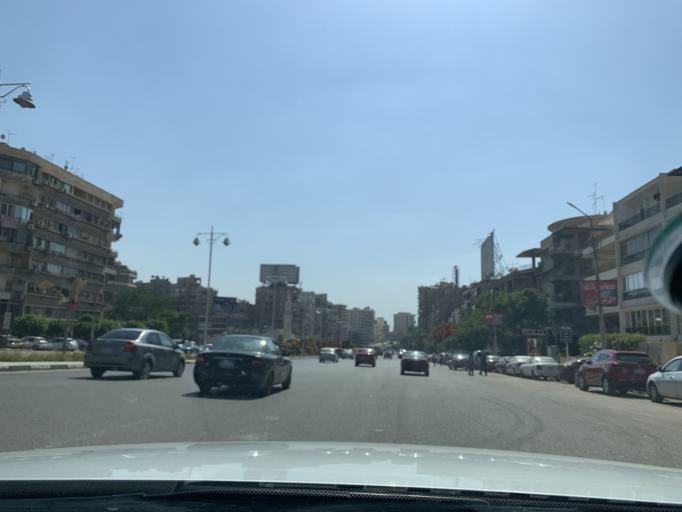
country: EG
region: Muhafazat al Qahirah
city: Cairo
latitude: 30.0850
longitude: 31.3308
